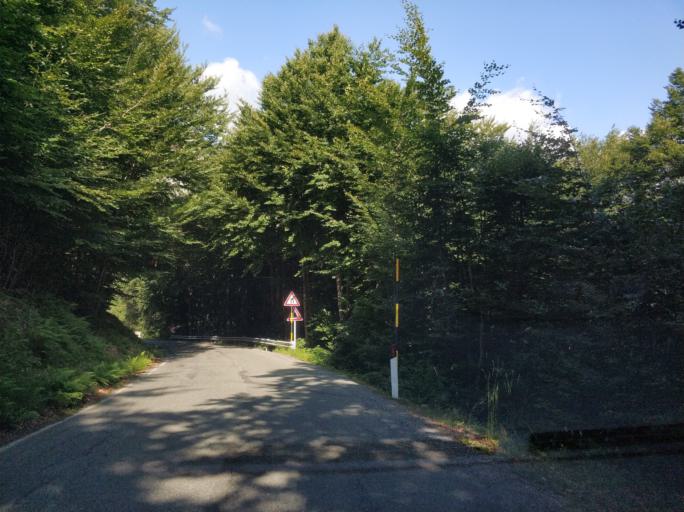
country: IT
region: Piedmont
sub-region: Provincia di Torino
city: Rubiana
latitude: 45.1815
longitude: 7.3781
